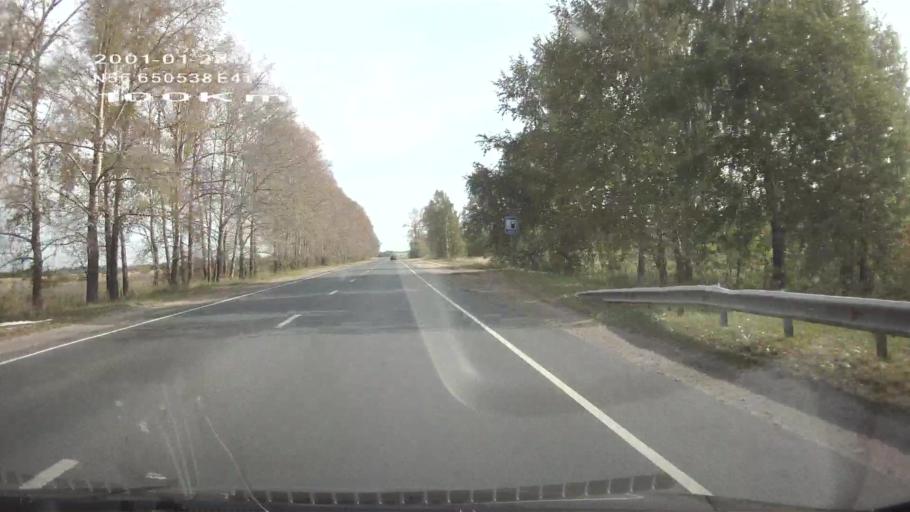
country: RU
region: Mariy-El
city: Yoshkar-Ola
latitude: 56.6505
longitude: 47.9468
